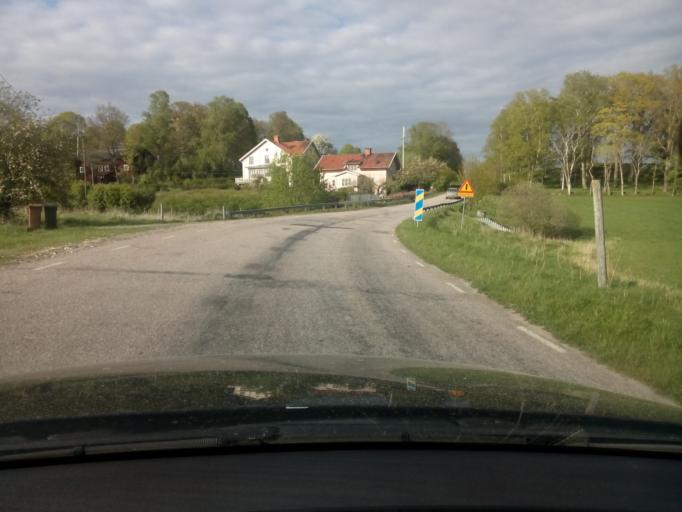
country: SE
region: Soedermanland
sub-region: Nykopings Kommun
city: Stigtomta
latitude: 58.9215
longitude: 16.8802
